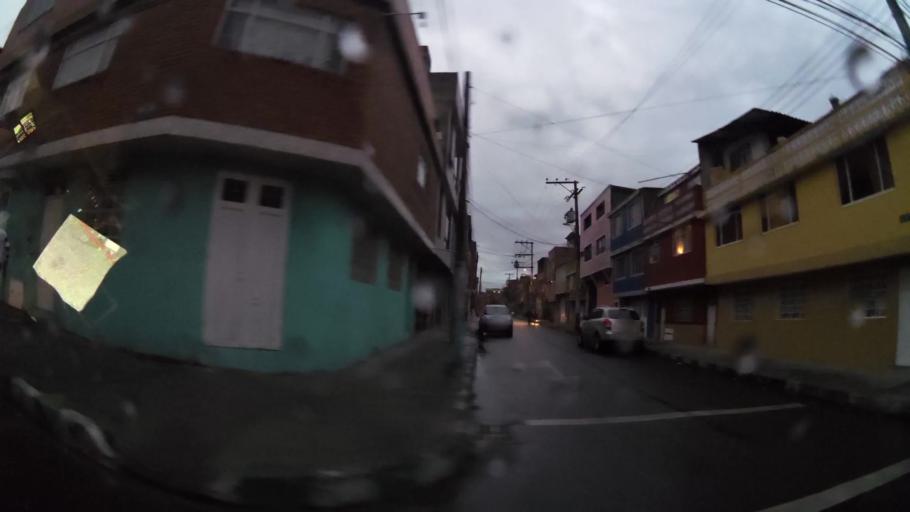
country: CO
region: Bogota D.C.
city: Bogota
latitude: 4.5825
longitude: -74.1414
